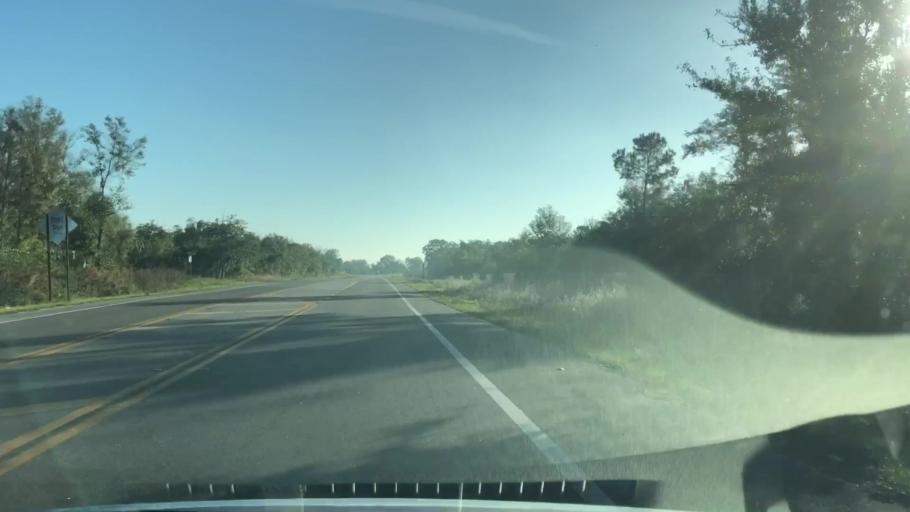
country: US
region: Florida
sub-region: Seminole County
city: Midway
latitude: 28.7856
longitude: -81.2533
